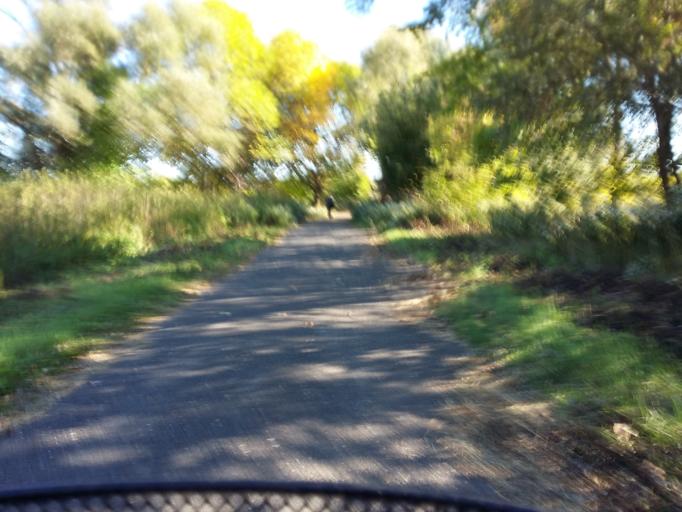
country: AT
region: Lower Austria
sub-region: Politischer Bezirk Ganserndorf
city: Marchegg
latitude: 48.2754
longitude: 16.9513
